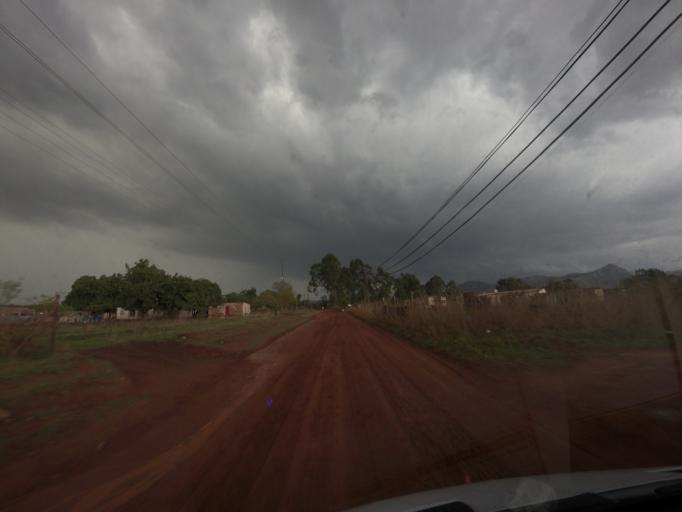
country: SZ
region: Hhohho
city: Lobamba
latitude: -26.4678
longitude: 31.2100
